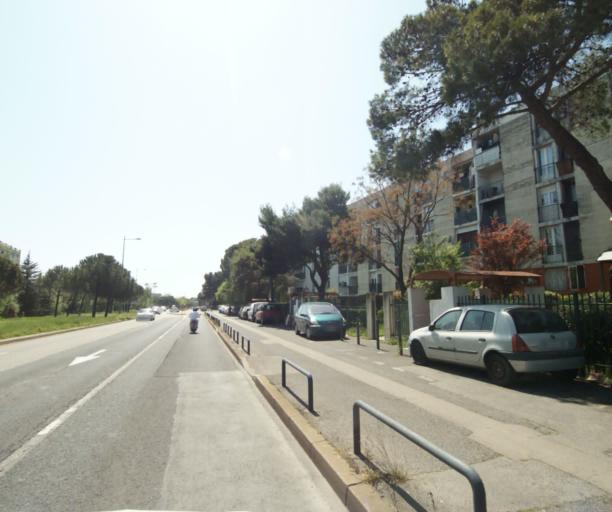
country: FR
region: Languedoc-Roussillon
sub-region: Departement de l'Herault
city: Juvignac
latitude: 43.6292
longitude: 3.8223
